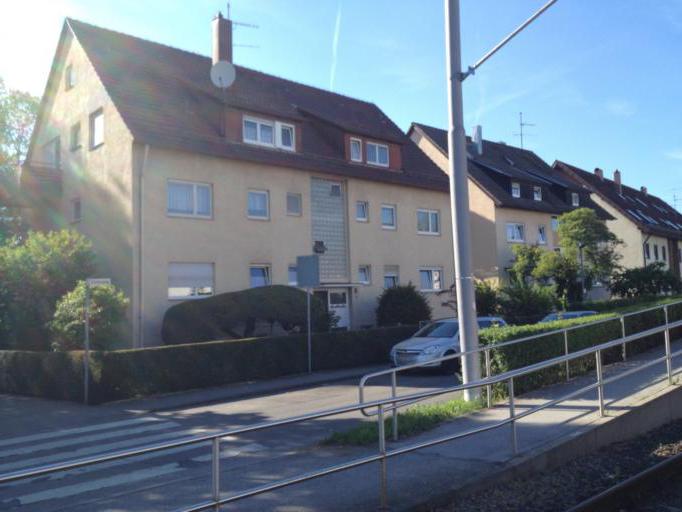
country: DE
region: Baden-Wuerttemberg
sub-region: Regierungsbezirk Stuttgart
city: Leinfelden-Echterdingen
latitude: 48.7033
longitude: 9.1433
